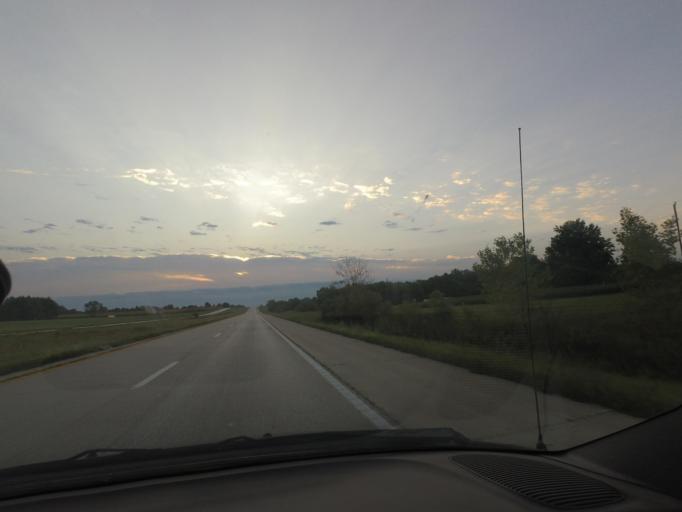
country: US
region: Missouri
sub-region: Macon County
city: Macon
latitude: 39.7506
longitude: -92.3807
